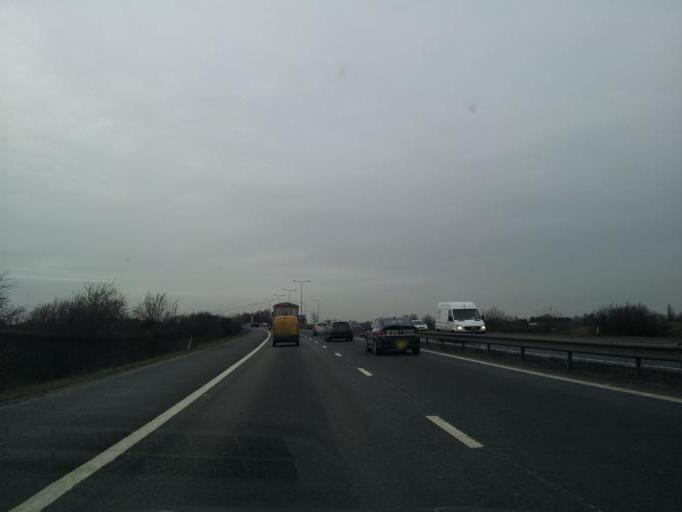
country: GB
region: England
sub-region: Cambridgeshire
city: Girton
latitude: 52.2233
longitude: 0.0774
